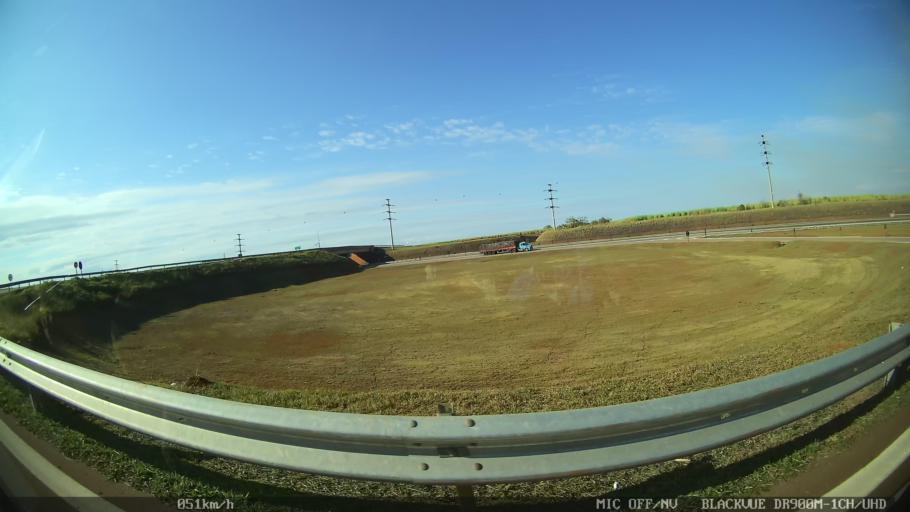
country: BR
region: Sao Paulo
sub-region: Piracicaba
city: Piracicaba
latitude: -22.6820
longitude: -47.5963
